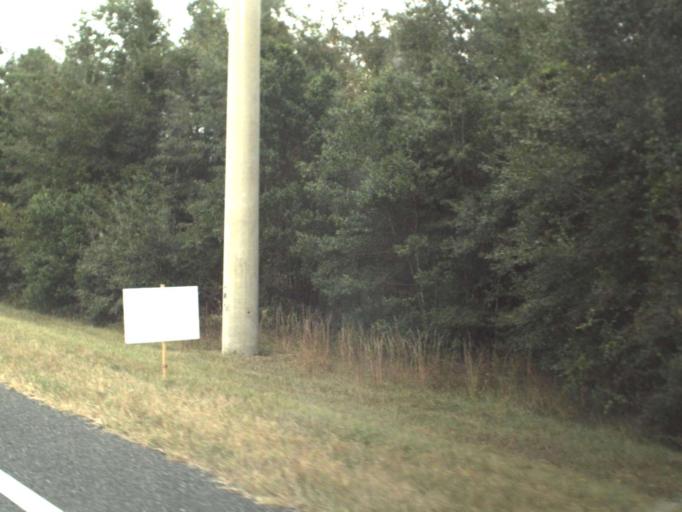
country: US
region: Florida
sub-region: Leon County
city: Tallahassee
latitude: 30.4227
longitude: -84.1114
